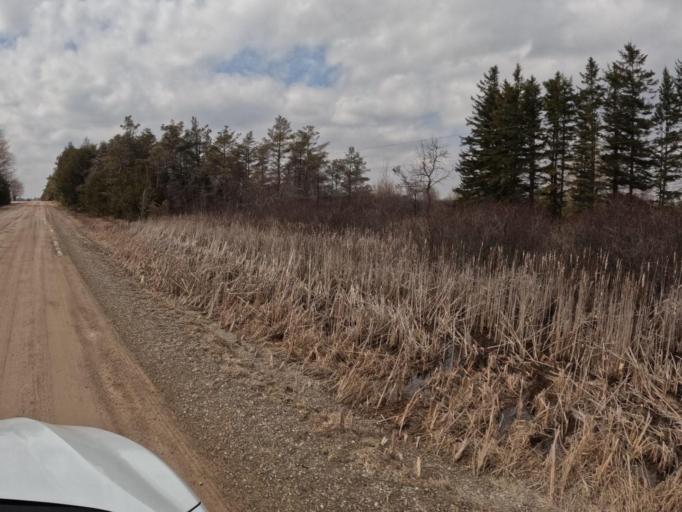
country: CA
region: Ontario
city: Shelburne
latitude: 44.0307
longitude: -80.2401
